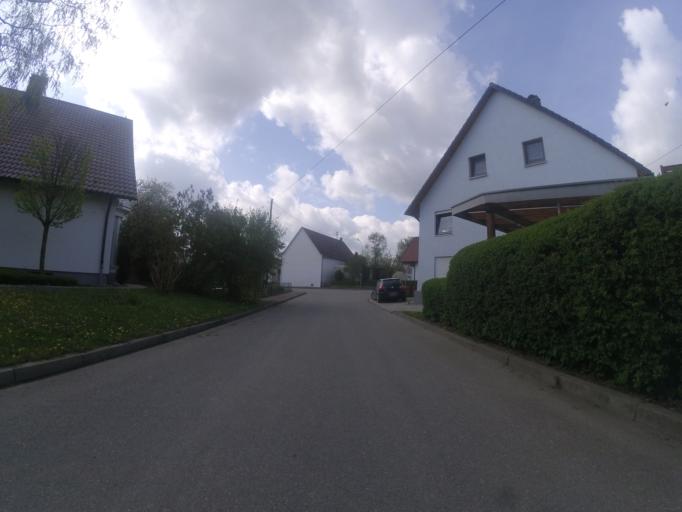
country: DE
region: Baden-Wuerttemberg
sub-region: Tuebingen Region
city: Griesingen
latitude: 48.2408
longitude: 9.7685
